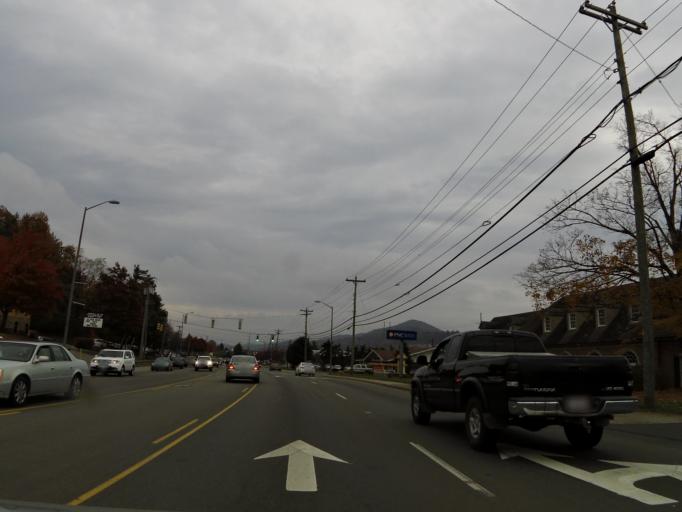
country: US
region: North Carolina
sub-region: Watauga County
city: Boone
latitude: 36.2043
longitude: -81.6678
